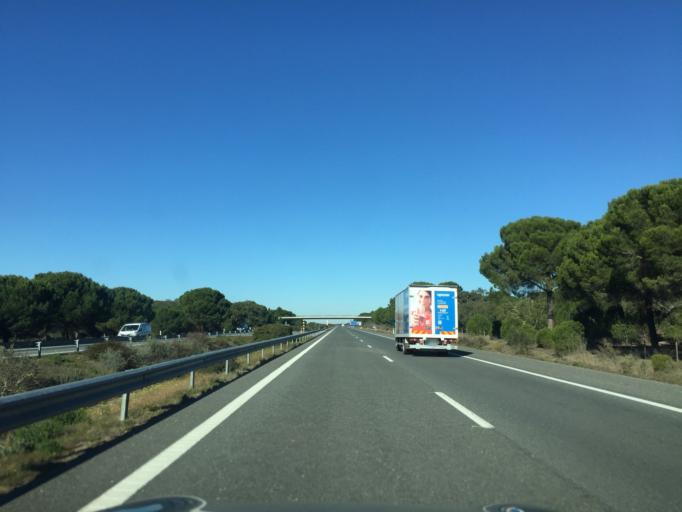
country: PT
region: Setubal
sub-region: Grandola
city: Grandola
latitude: 38.1501
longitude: -8.4654
